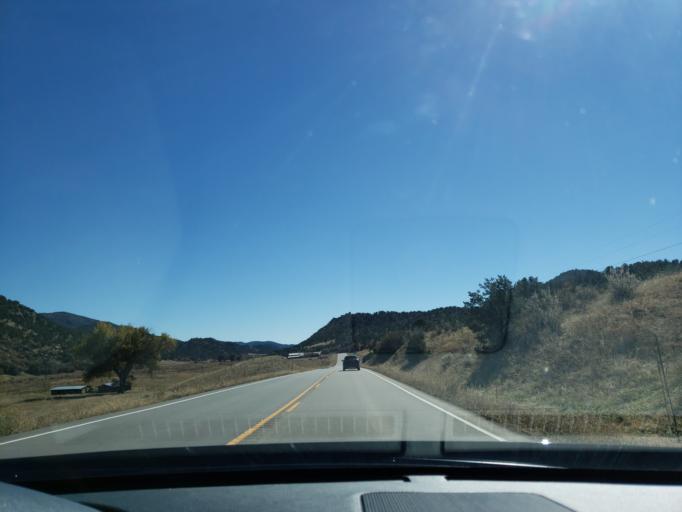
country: US
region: Colorado
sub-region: Fremont County
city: Canon City
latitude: 38.6092
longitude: -105.4394
